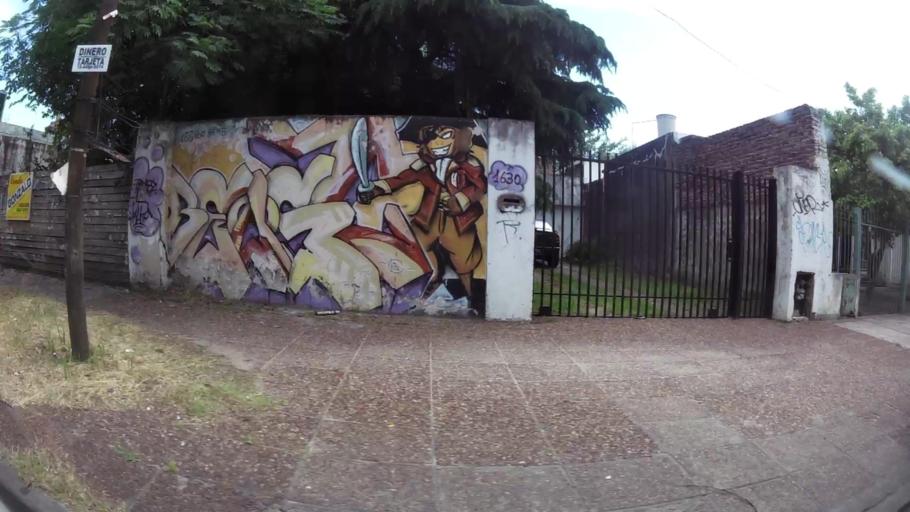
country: AR
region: Buenos Aires
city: Ituzaingo
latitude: -34.6464
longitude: -58.6809
